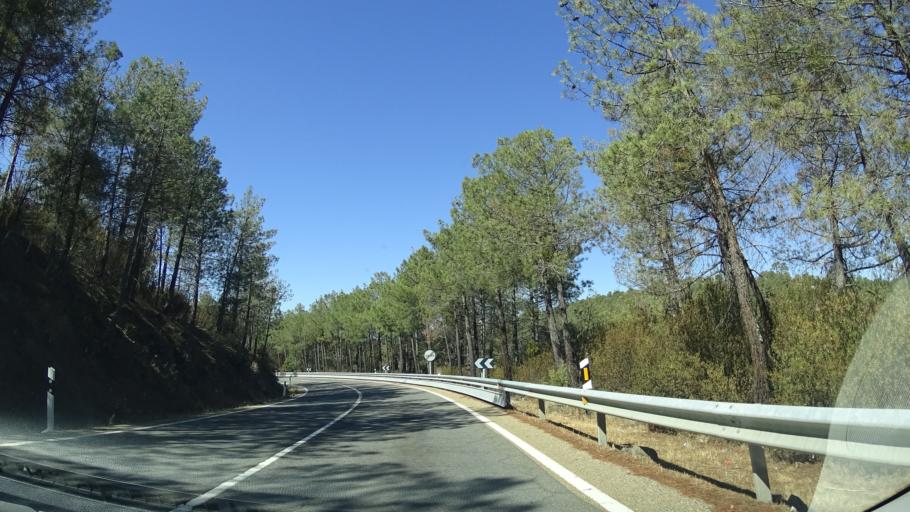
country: ES
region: Madrid
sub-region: Provincia de Madrid
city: Valdemaqueda
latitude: 40.5567
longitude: -4.2867
